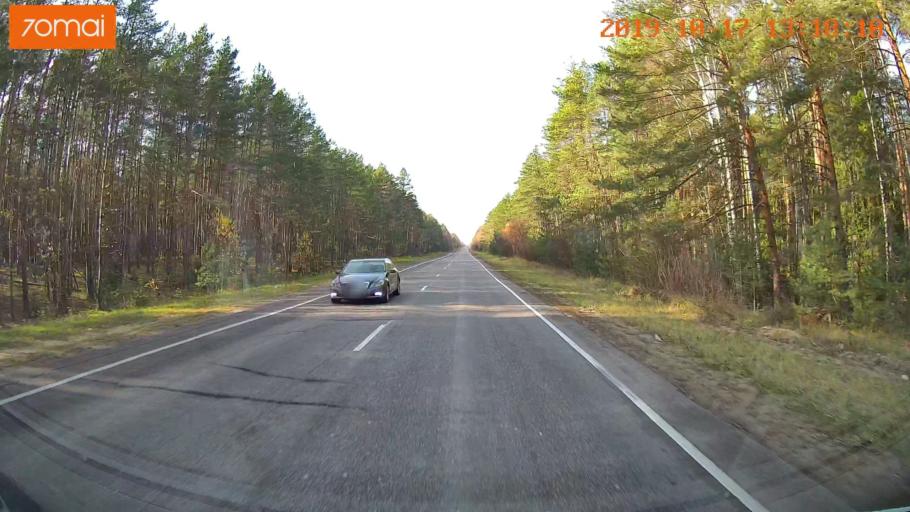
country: RU
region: Rjazan
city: Gus'-Zheleznyy
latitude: 55.0612
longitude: 41.1042
